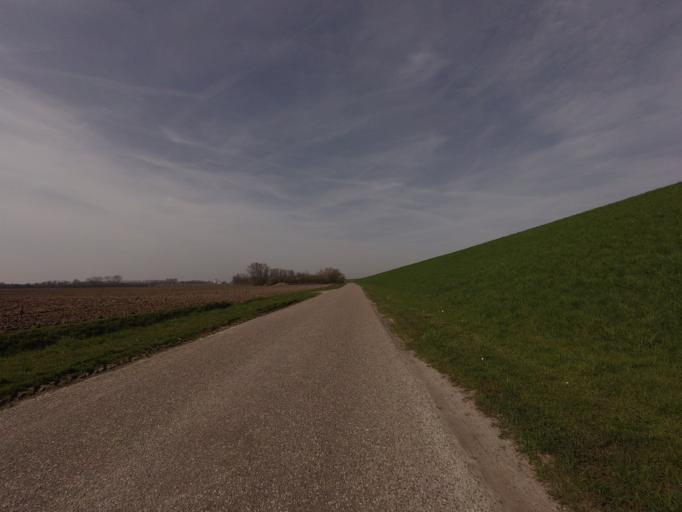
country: NL
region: Zeeland
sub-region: Gemeente Hulst
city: Hulst
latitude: 51.3720
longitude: 4.0424
